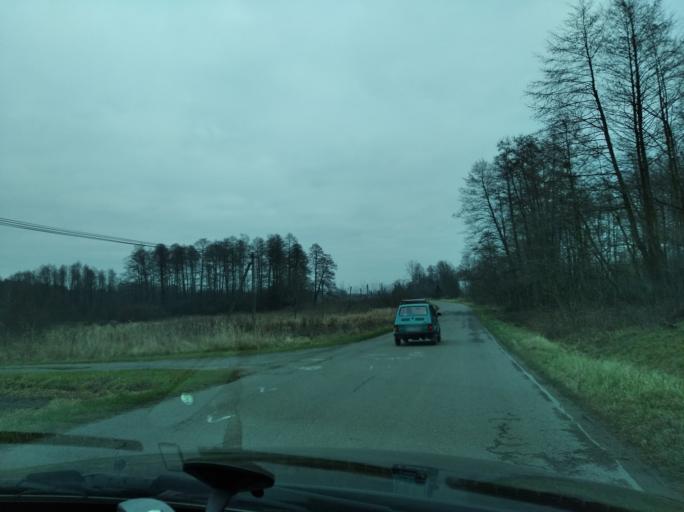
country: PL
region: Subcarpathian Voivodeship
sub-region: Powiat lancucki
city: Brzoza Stadnicka
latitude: 50.1933
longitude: 22.2641
